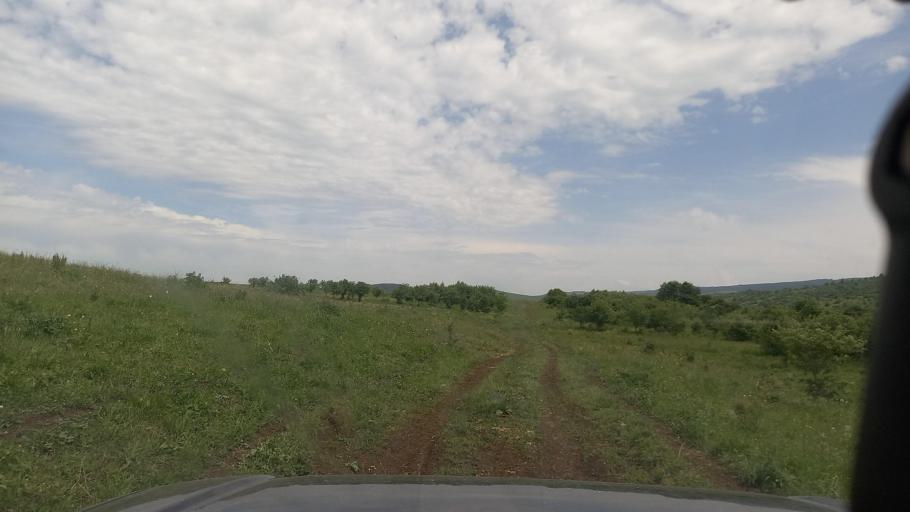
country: RU
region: Karachayevo-Cherkesiya
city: Pregradnaya
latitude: 44.0826
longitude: 41.2457
